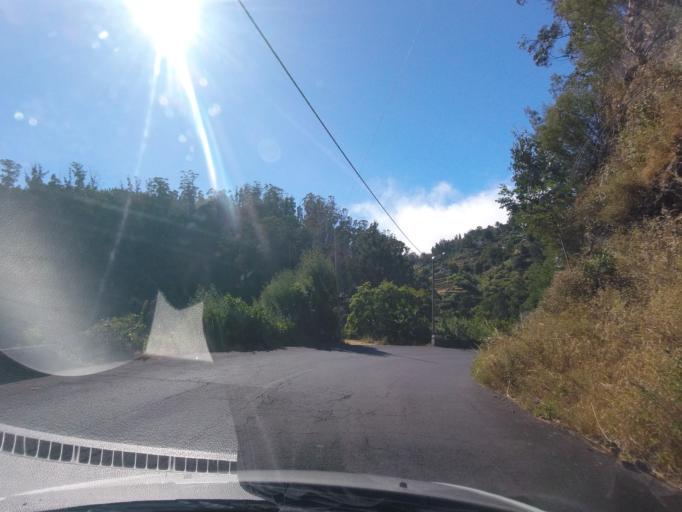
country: PT
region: Madeira
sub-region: Santa Cruz
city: Camacha
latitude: 32.6908
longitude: -16.8509
